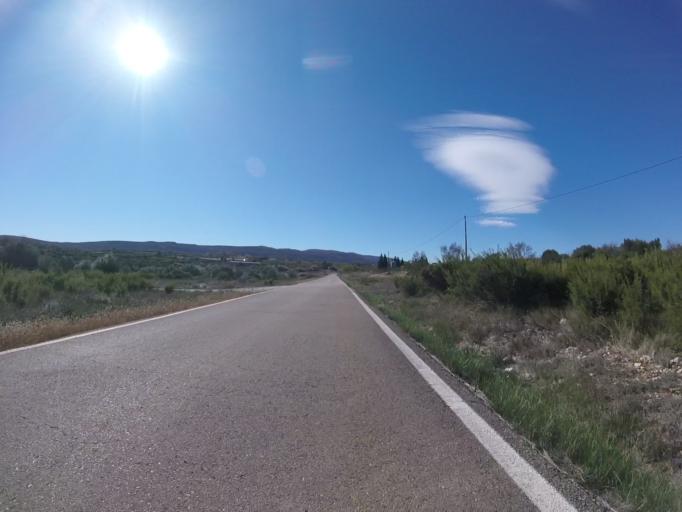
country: ES
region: Valencia
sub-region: Provincia de Castello
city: Albocasser
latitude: 40.3729
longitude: 0.0197
